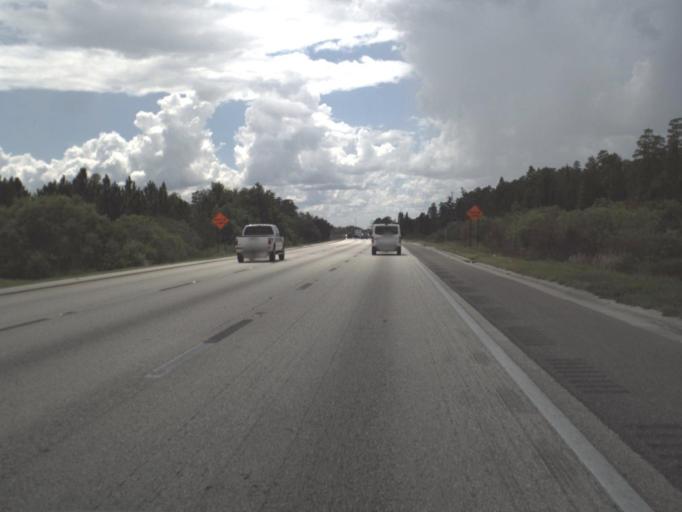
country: US
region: Florida
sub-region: Polk County
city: Lake Alfred
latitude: 28.1950
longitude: -81.7136
